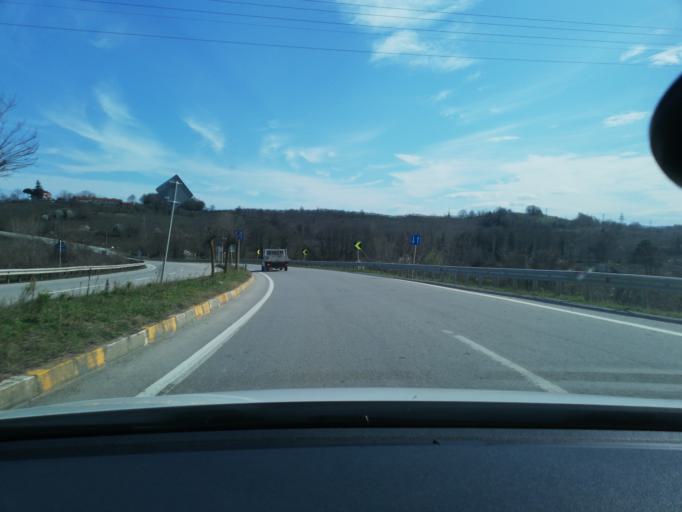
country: TR
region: Duzce
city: Akcakoca
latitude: 41.0831
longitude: 31.1456
